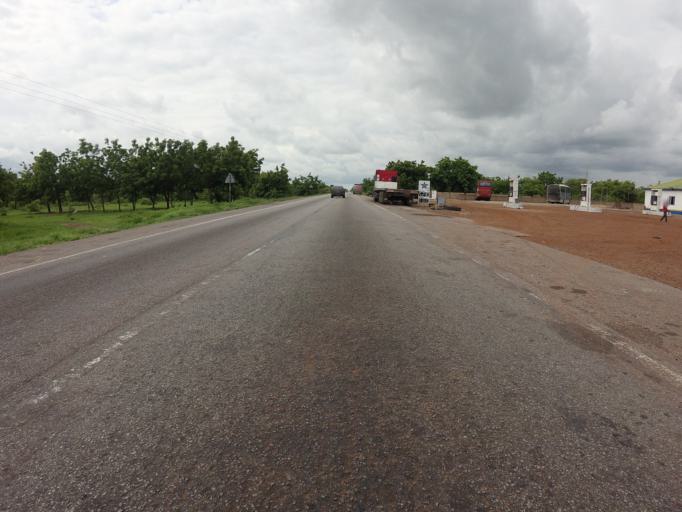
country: GH
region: Northern
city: Tamale
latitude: 8.9842
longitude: -1.3560
